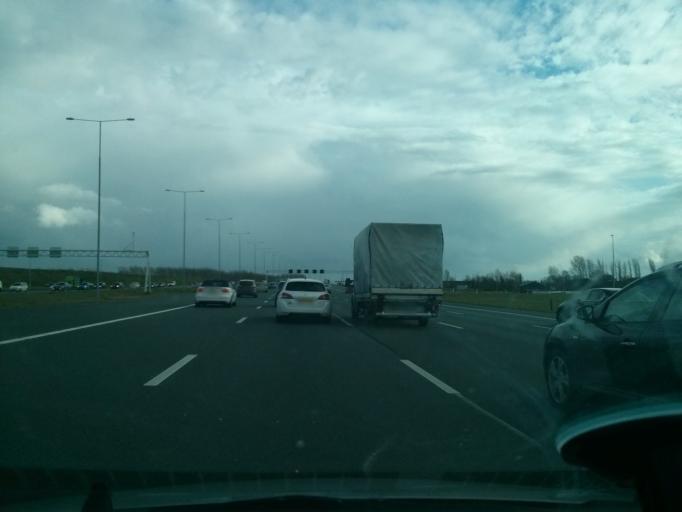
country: NL
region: North Holland
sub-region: Gemeente Amsterdam
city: Amsterdam-Zuidoost
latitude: 52.2650
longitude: 4.9620
